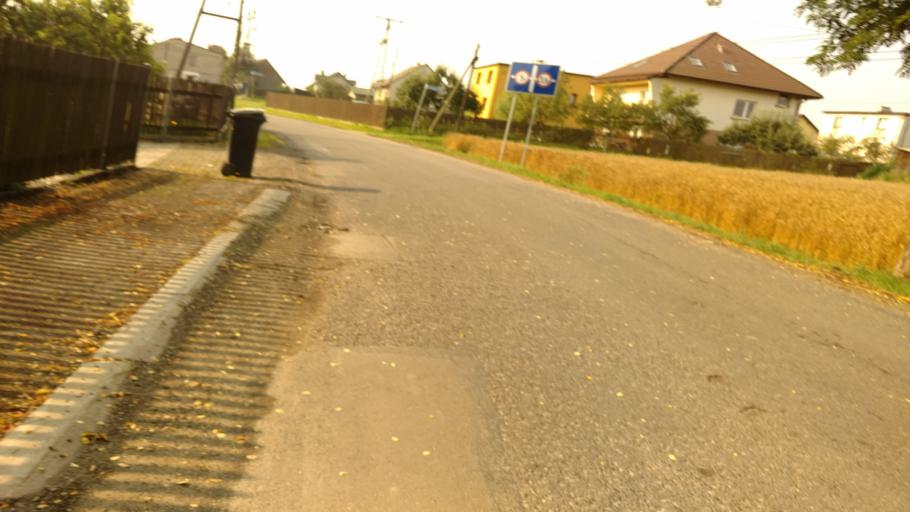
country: PL
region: Silesian Voivodeship
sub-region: Powiat pszczynski
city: Jankowice
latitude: 50.0240
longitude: 18.9784
